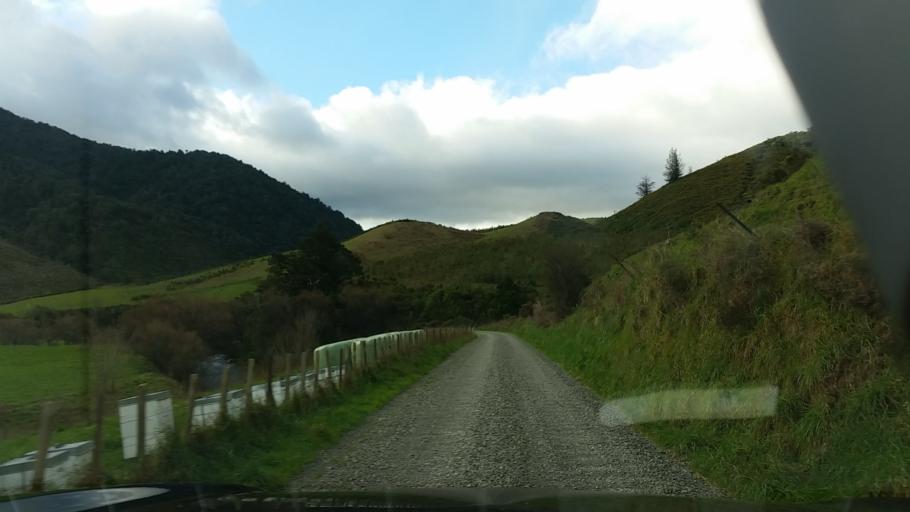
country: NZ
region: Nelson
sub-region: Nelson City
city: Nelson
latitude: -41.1924
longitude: 173.6366
